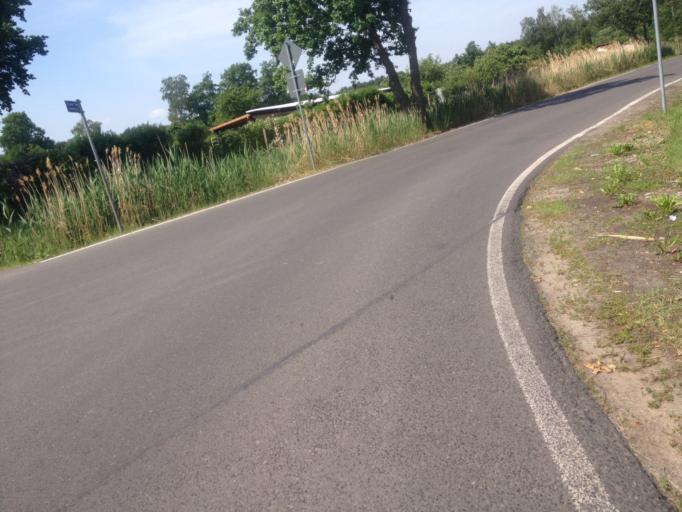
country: DE
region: Brandenburg
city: Cottbus
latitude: 51.8133
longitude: 14.3332
